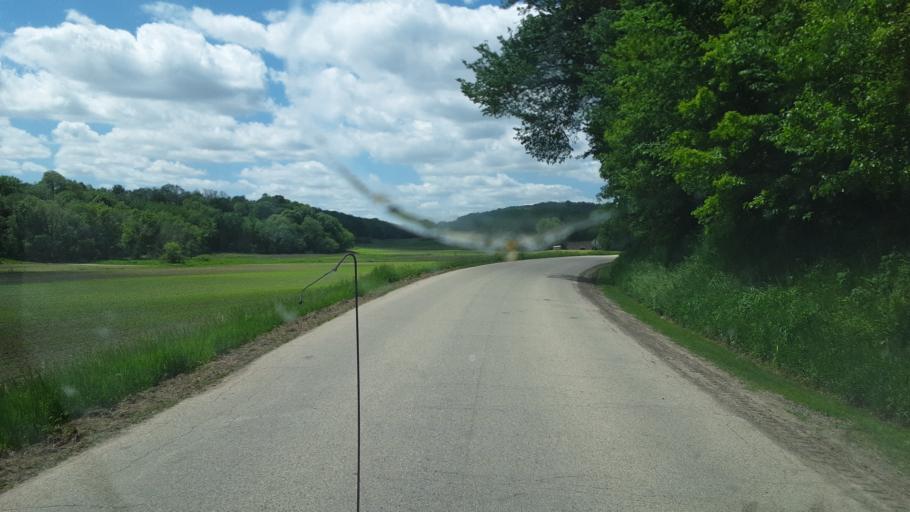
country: US
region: Wisconsin
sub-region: Sauk County
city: Reedsburg
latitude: 43.5756
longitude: -90.0010
